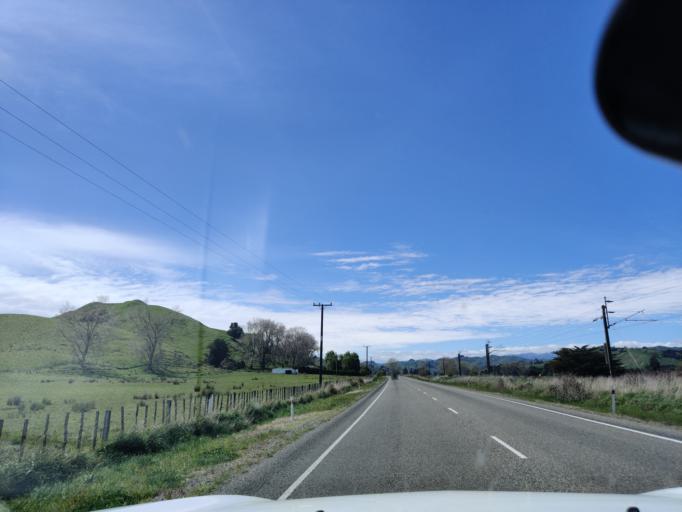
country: NZ
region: Manawatu-Wanganui
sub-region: Ruapehu District
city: Waiouru
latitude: -39.8562
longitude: 175.7228
